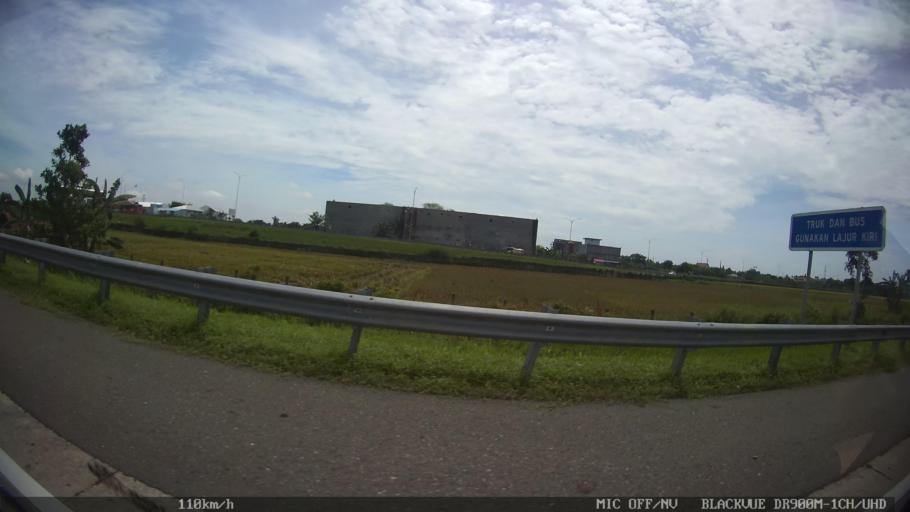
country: ID
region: North Sumatra
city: Percut
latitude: 3.5574
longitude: 98.8522
